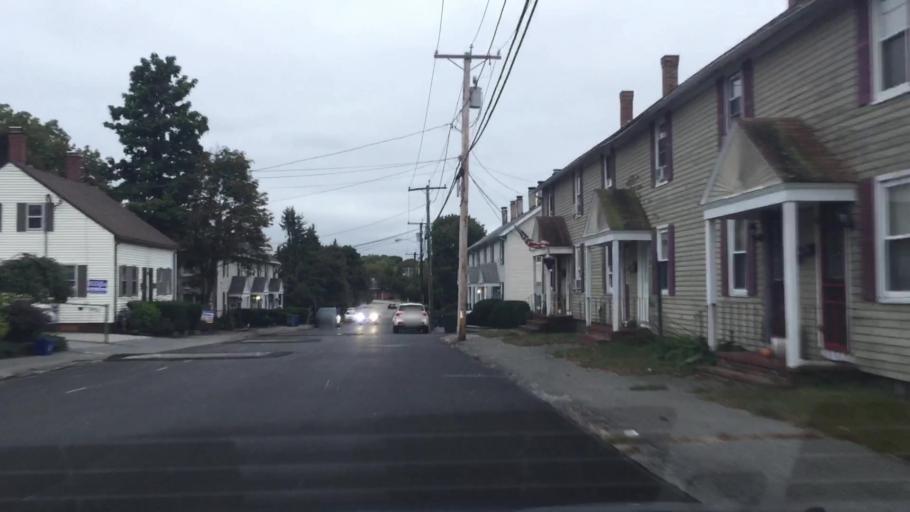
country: US
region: Massachusetts
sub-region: Essex County
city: North Andover
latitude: 42.7001
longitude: -71.1238
